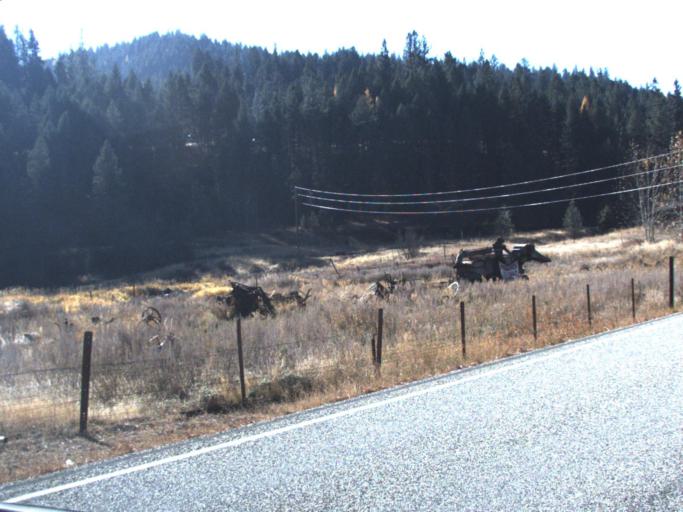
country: US
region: Washington
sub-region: Ferry County
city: Republic
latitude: 48.7835
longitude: -118.6242
